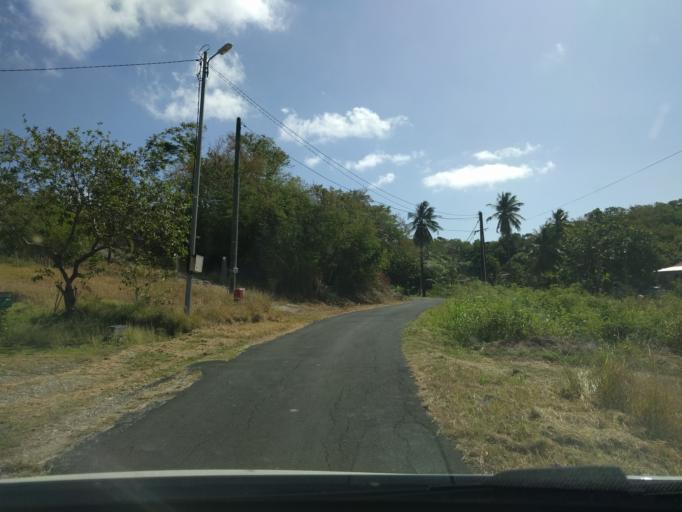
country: GP
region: Guadeloupe
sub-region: Guadeloupe
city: Grand-Bourg
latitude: 15.9756
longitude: -61.2570
